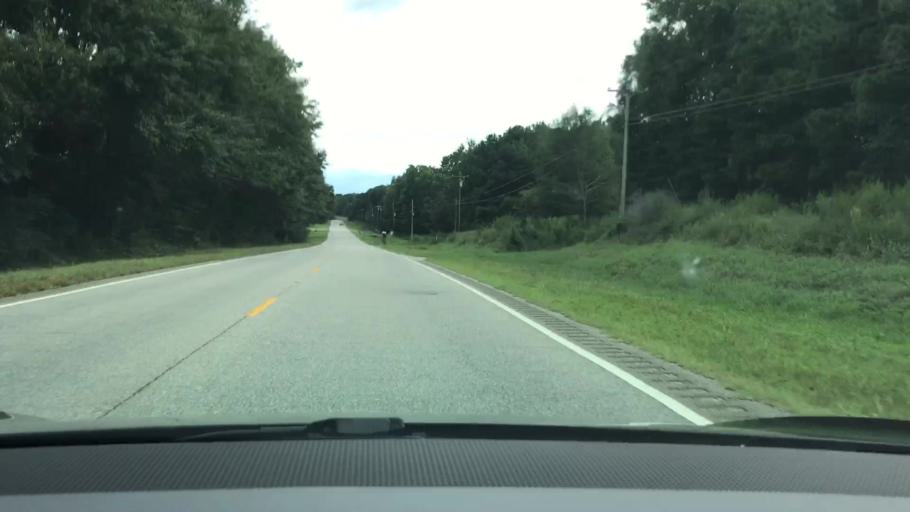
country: US
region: Alabama
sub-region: Coffee County
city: Elba
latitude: 31.6032
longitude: -86.0022
